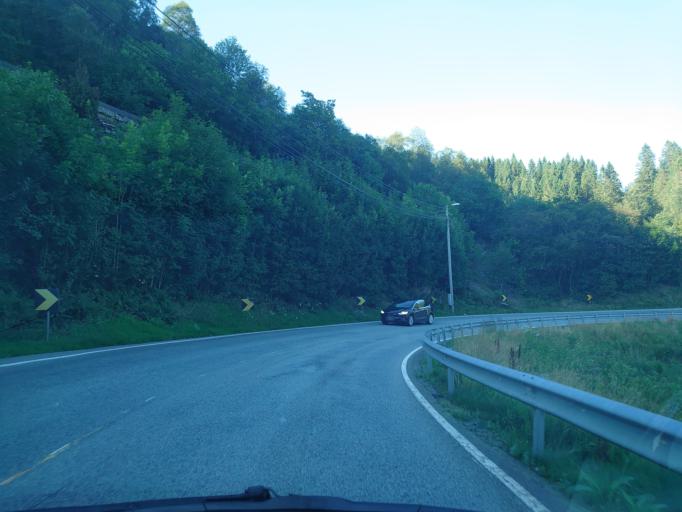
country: NO
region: Hordaland
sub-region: Bergen
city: Espeland
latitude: 60.3522
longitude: 5.4297
